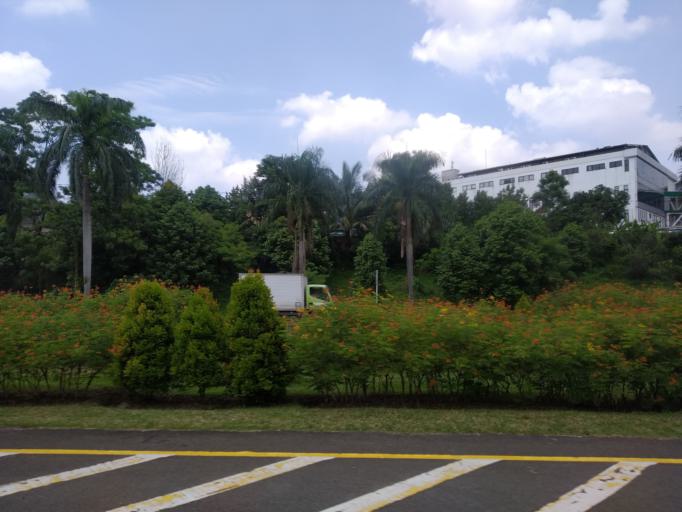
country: ID
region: West Java
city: Bogor
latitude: -6.6013
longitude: 106.8118
